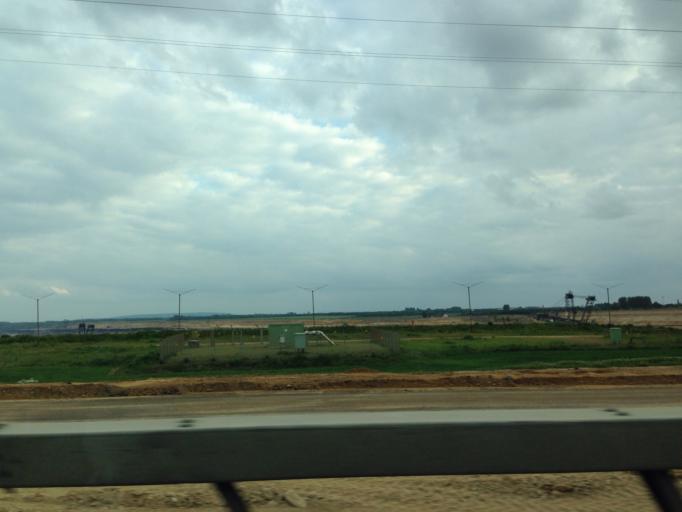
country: DE
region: North Rhine-Westphalia
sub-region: Regierungsbezirk Dusseldorf
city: Juchen
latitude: 51.0936
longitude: 6.4517
